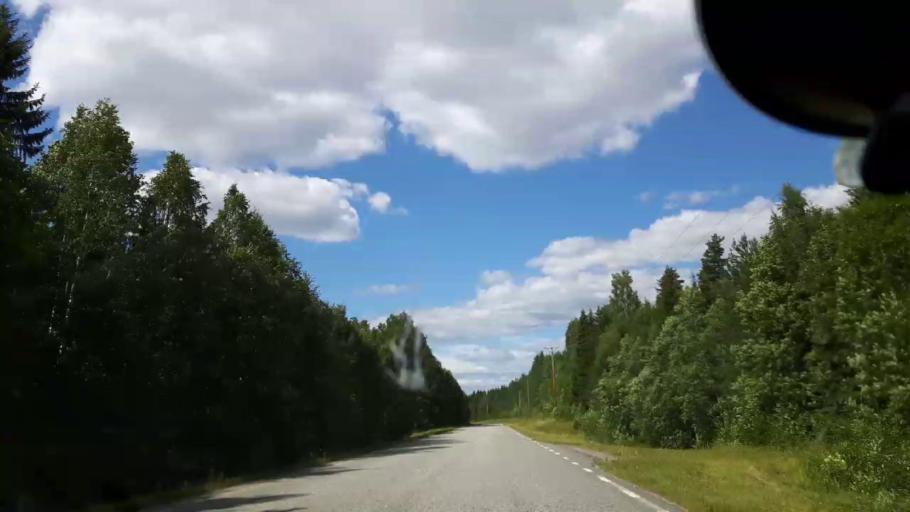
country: SE
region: Vaesternorrland
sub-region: Ange Kommun
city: Fransta
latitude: 62.7524
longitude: 16.3172
